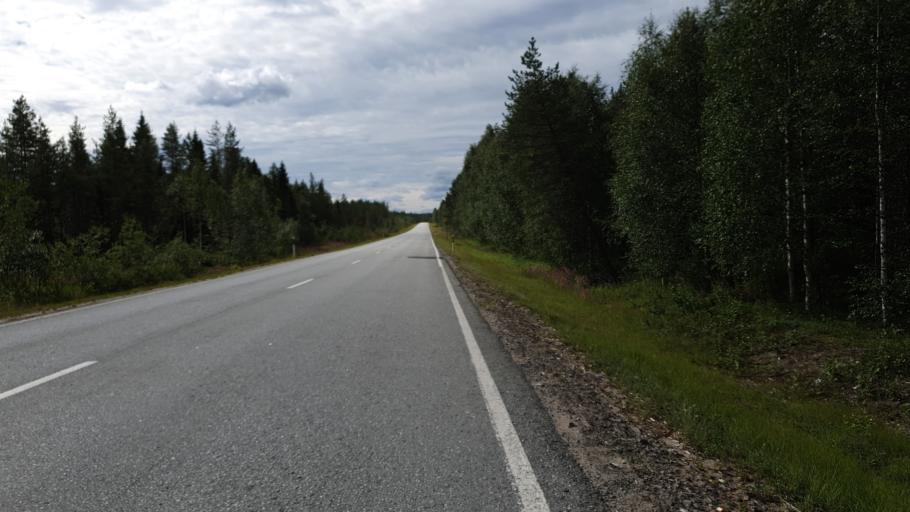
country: FI
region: Kainuu
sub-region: Kehys-Kainuu
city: Kuhmo
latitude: 64.5284
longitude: 29.9450
